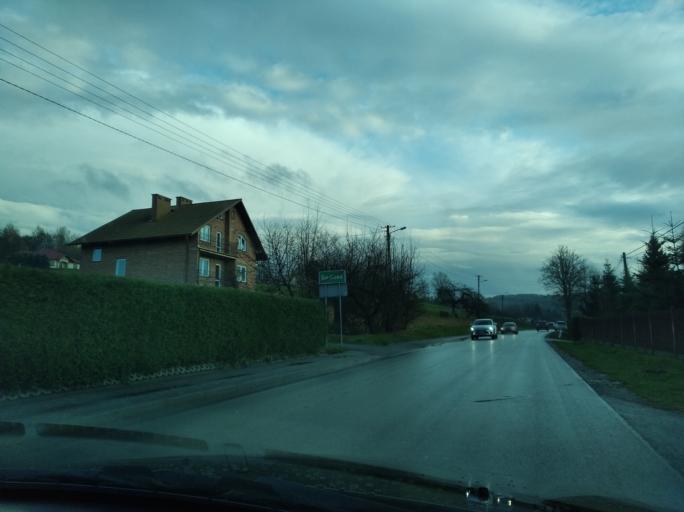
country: PL
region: Subcarpathian Voivodeship
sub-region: Powiat rzeszowski
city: Lubenia
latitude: 49.9348
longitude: 21.9211
